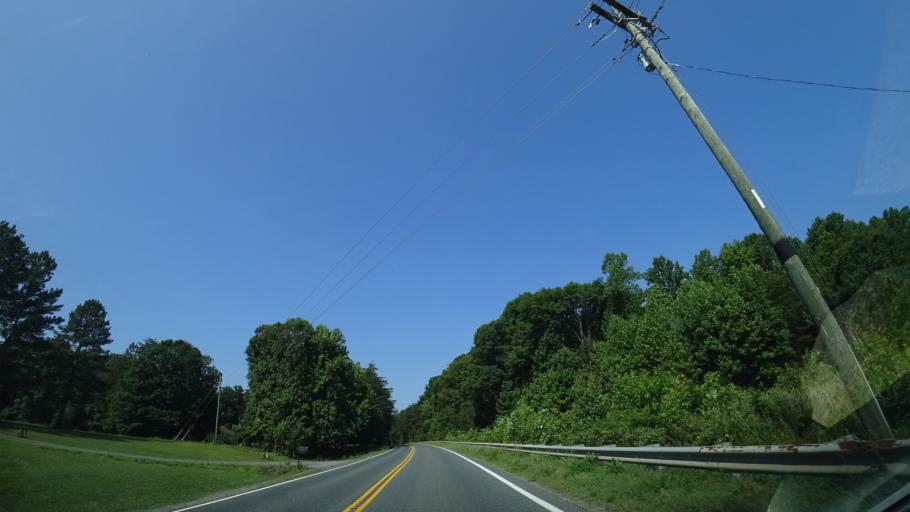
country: US
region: Virginia
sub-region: Louisa County
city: Louisa
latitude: 38.0844
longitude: -77.8272
